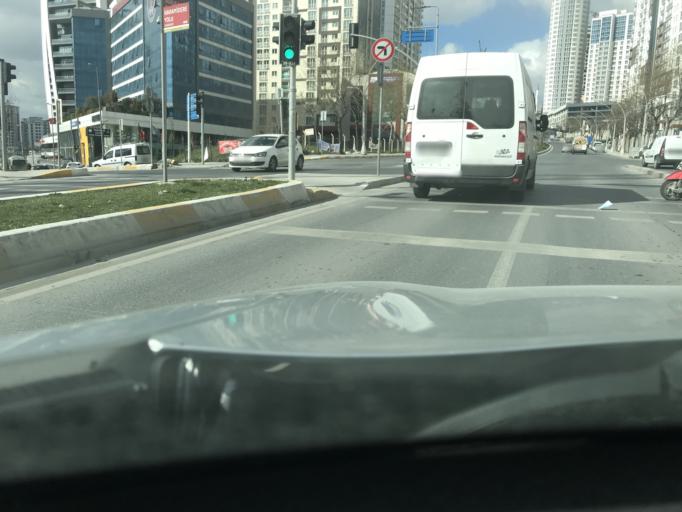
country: TR
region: Istanbul
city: Esenyurt
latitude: 41.0143
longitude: 28.6822
